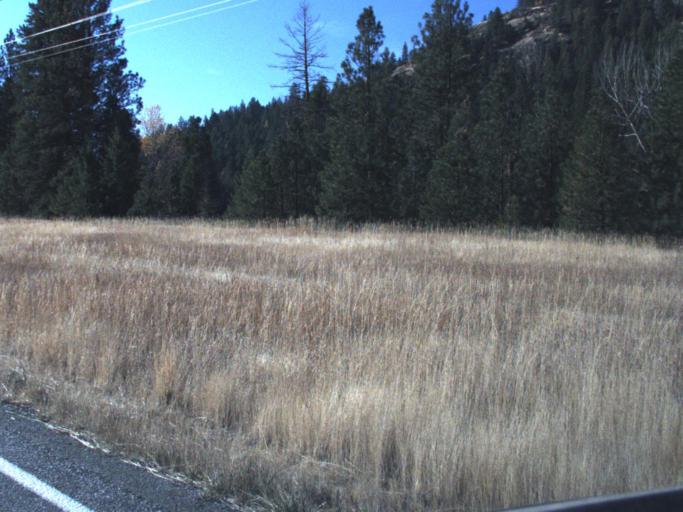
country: US
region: Washington
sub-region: Ferry County
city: Republic
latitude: 48.8103
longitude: -118.6009
